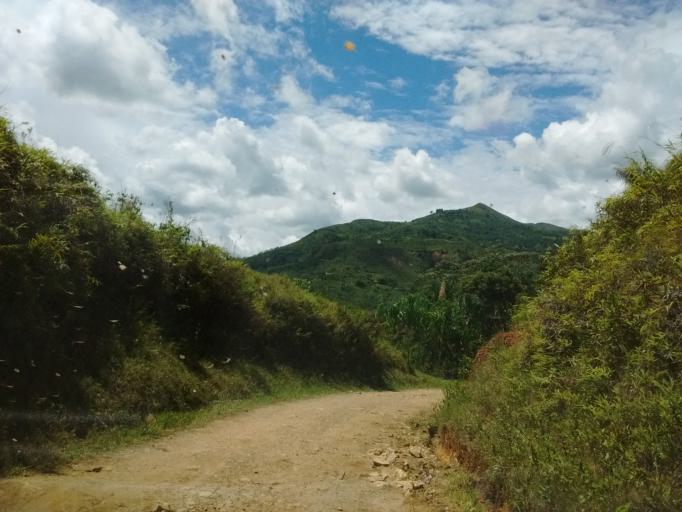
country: CO
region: Cauca
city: Villa Rica
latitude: 2.6350
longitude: -76.7709
